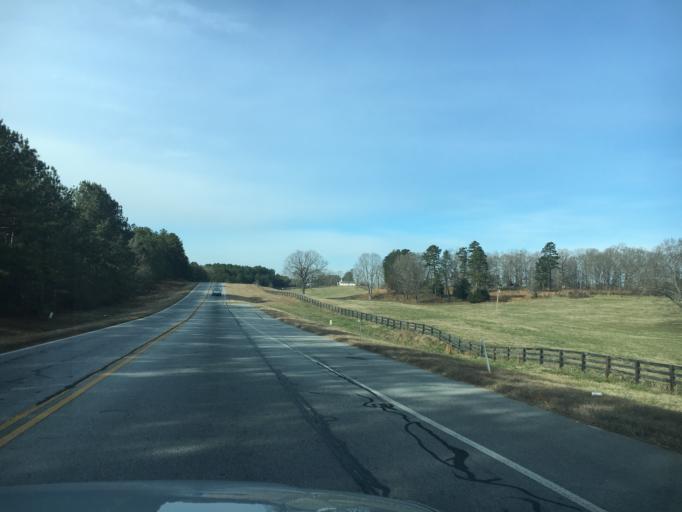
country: US
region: Georgia
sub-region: Jackson County
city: Hoschton
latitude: 34.0754
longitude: -83.7388
